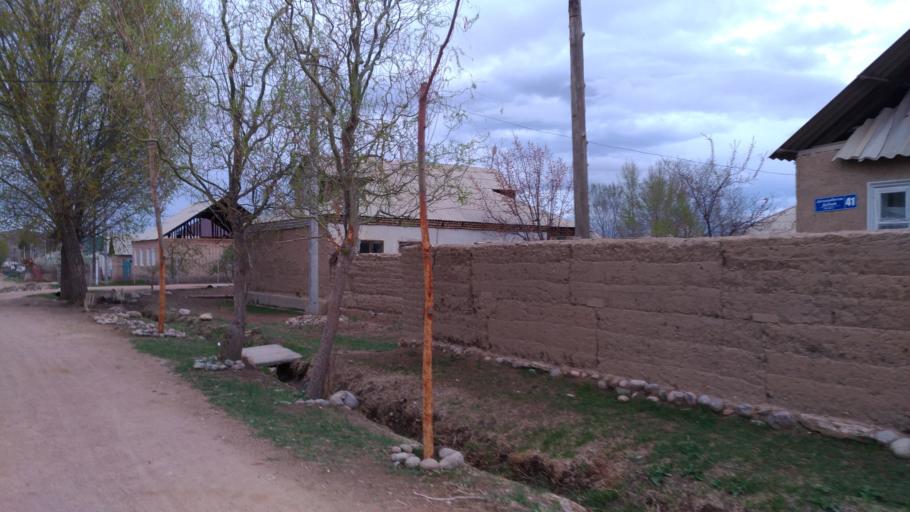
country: KG
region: Ysyk-Koel
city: Bokombayevskoye
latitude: 42.1124
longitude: 76.9833
